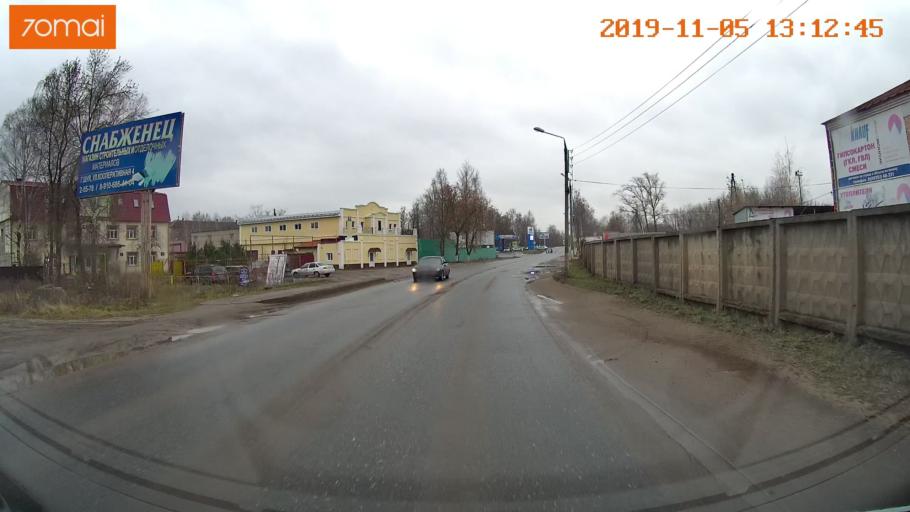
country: RU
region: Ivanovo
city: Shuya
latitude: 56.8557
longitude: 41.3531
